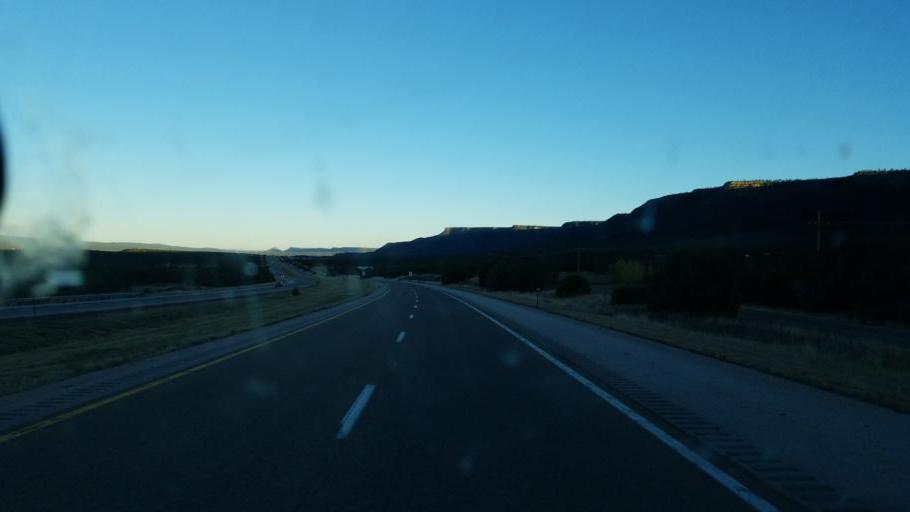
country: US
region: New Mexico
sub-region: San Miguel County
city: Pecos
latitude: 35.4298
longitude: -105.5974
